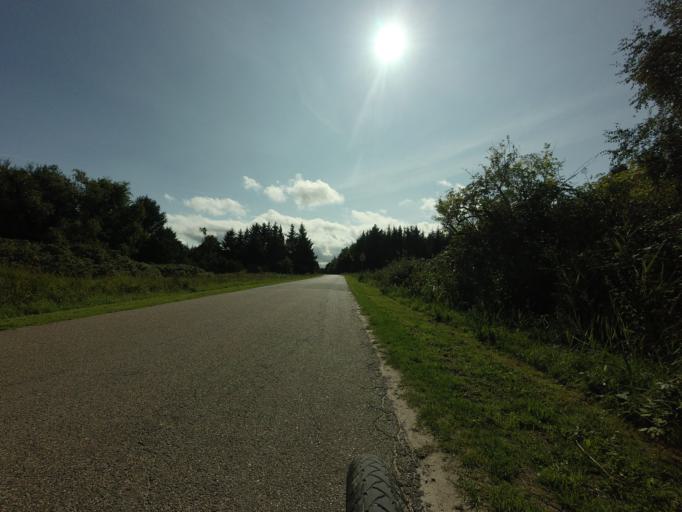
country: DK
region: North Denmark
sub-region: Hjorring Kommune
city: Hirtshals
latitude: 57.5826
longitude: 10.0284
